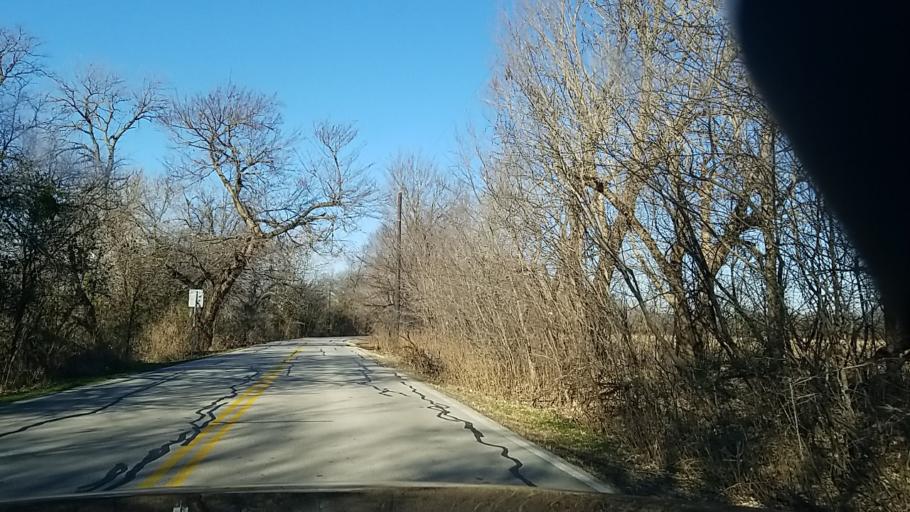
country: US
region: Texas
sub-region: Denton County
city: Argyle
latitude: 33.1491
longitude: -97.1383
